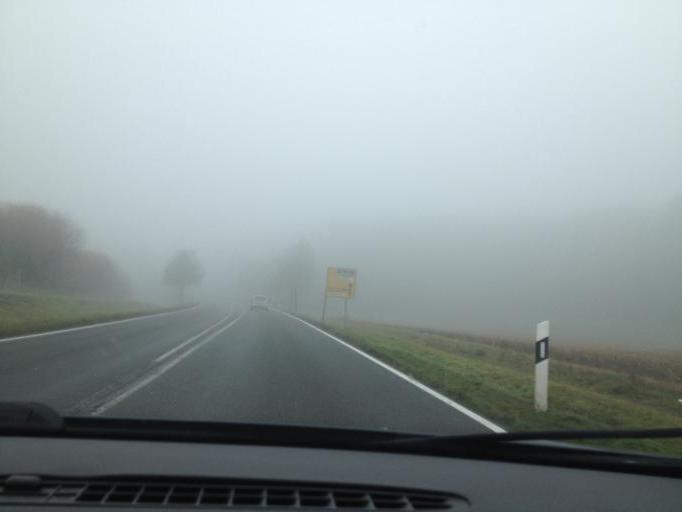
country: DE
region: Rheinland-Pfalz
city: Mackenbach
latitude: 49.4774
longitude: 7.6010
